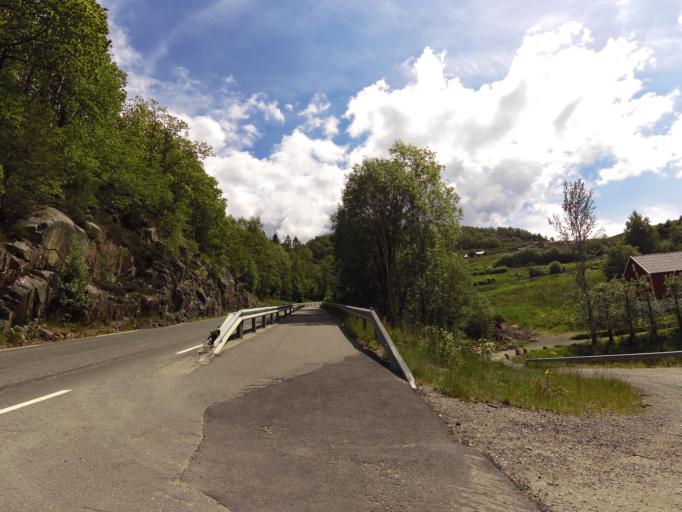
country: NO
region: Vest-Agder
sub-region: Lyngdal
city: Lyngdal
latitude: 58.1168
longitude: 7.0628
